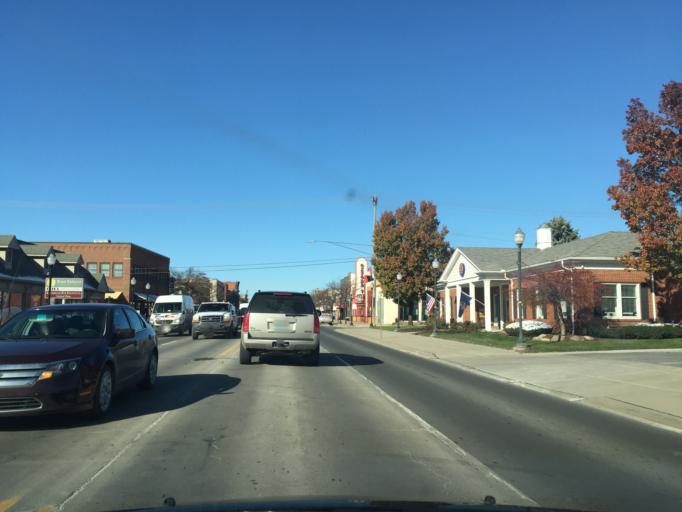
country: US
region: Michigan
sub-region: Oakland County
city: Oxford
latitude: 42.8229
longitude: -83.2632
